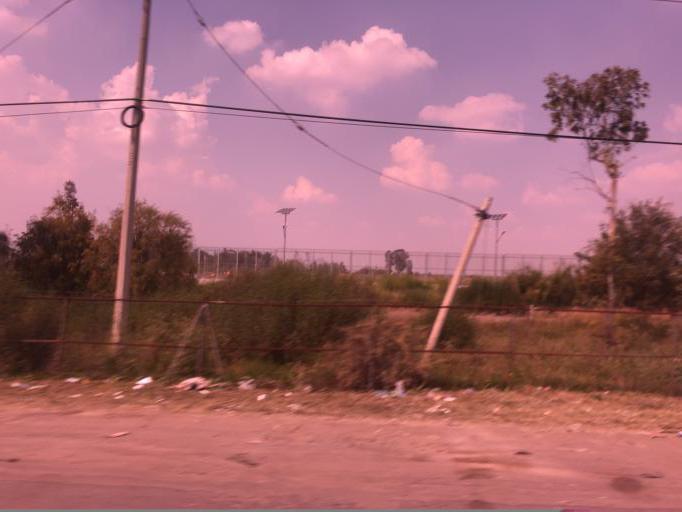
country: MX
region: Mexico
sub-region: Ciudad Nezahualcoyotl
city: Colonia Gustavo Baz Prada
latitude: 19.4694
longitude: -99.0049
